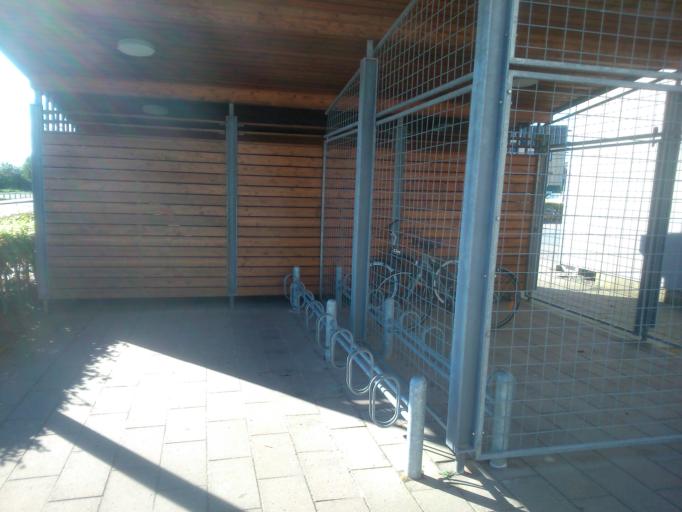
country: DK
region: North Denmark
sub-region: Thisted Kommune
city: Thisted
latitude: 56.9516
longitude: 8.6949
